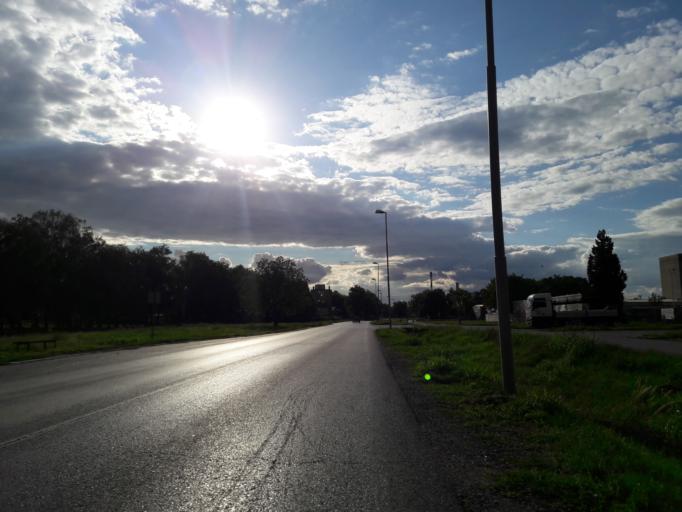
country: HR
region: Osjecko-Baranjska
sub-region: Grad Osijek
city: Osijek
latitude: 45.5445
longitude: 18.7357
